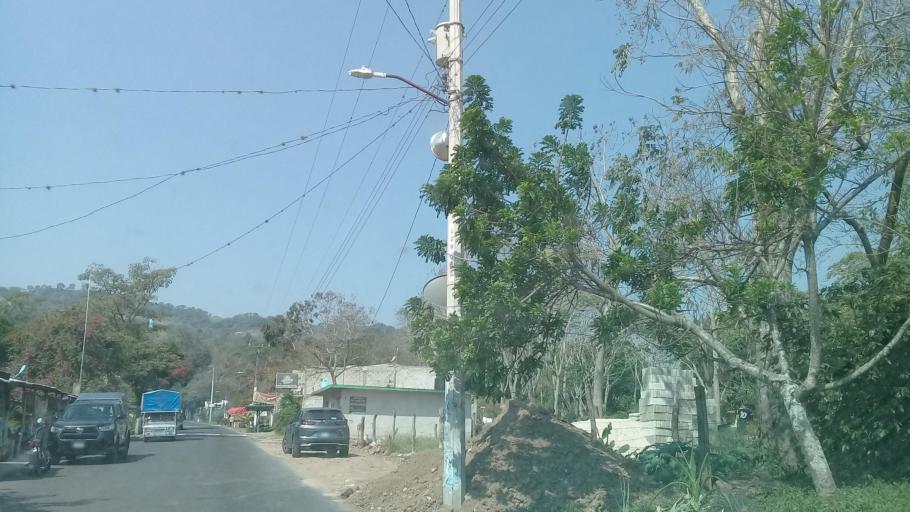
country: MX
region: Veracruz
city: El Castillo
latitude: 19.5721
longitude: -96.8342
